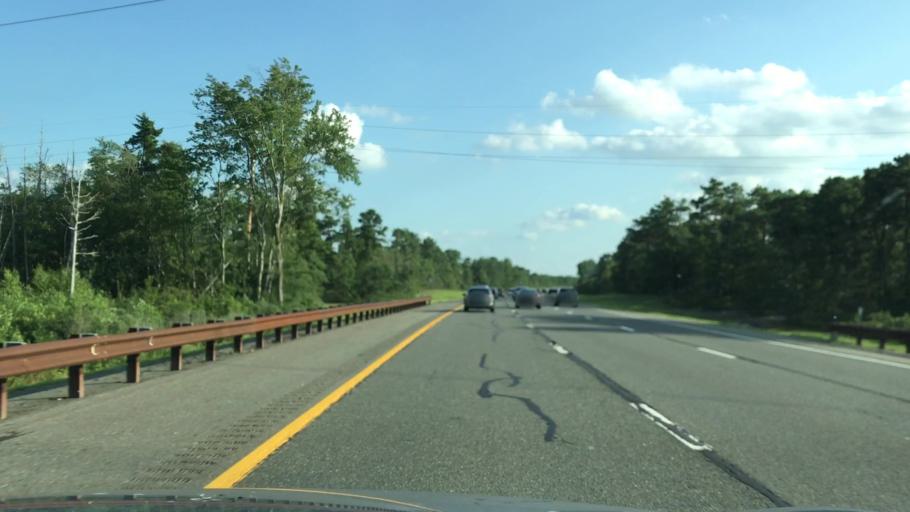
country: US
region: New Jersey
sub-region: Ocean County
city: Waretown
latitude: 39.8189
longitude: -74.2293
